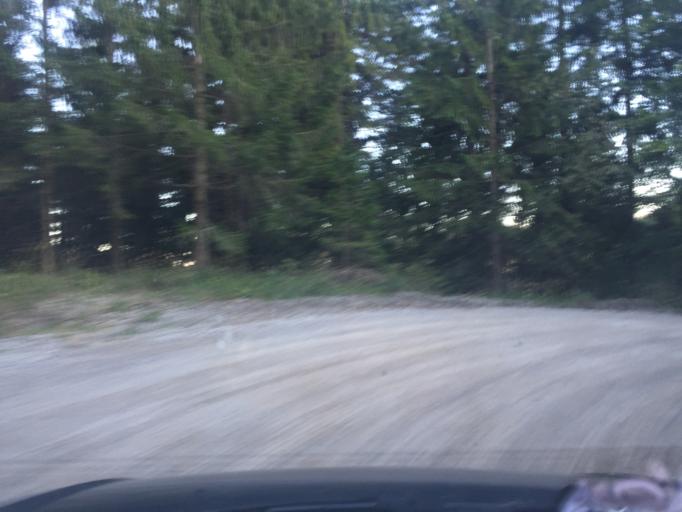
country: SI
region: Ravne na Koroskem
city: Kotlje
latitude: 46.4625
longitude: 14.9959
